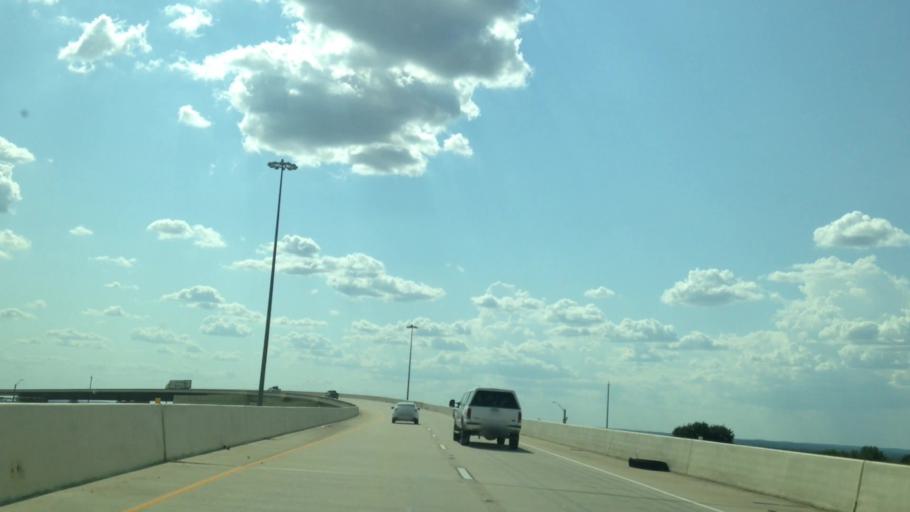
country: US
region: Texas
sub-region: Travis County
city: Onion Creek
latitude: 30.1121
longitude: -97.8038
